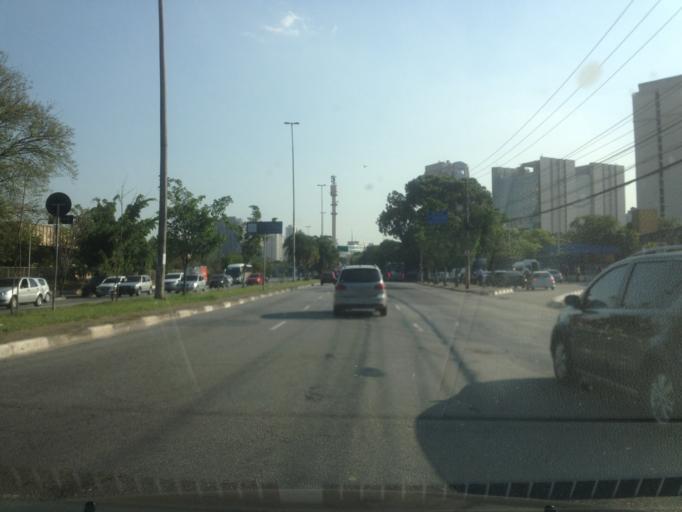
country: BR
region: Sao Paulo
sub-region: Sao Paulo
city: Sao Paulo
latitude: -23.5205
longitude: -46.6576
